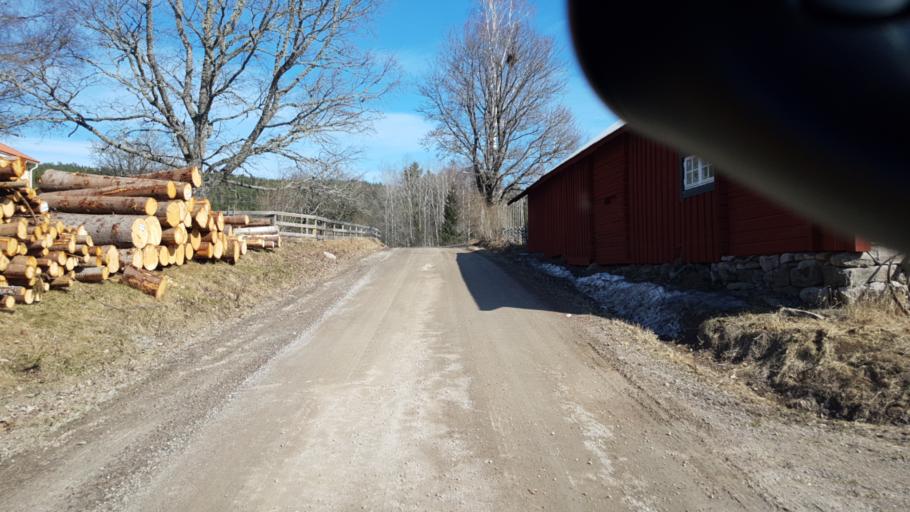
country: SE
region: Vaermland
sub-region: Arvika Kommun
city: Arvika
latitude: 59.6881
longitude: 12.7827
